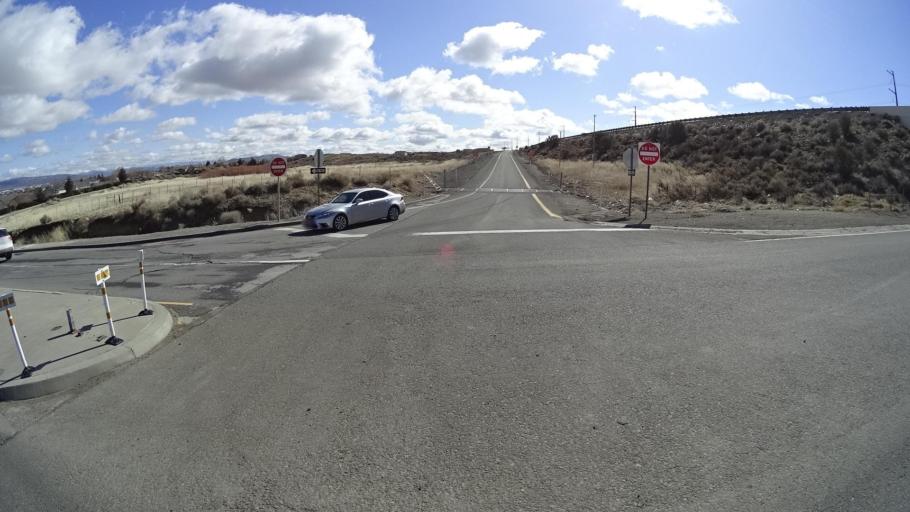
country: US
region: Nevada
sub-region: Washoe County
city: Lemmon Valley
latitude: 39.6255
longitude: -119.9196
